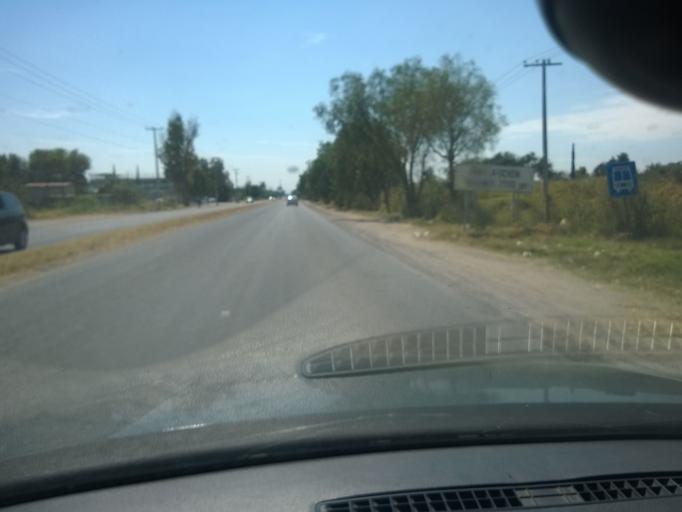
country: MX
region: Guanajuato
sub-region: Leon
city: El CERESO
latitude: 20.9964
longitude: -101.7031
